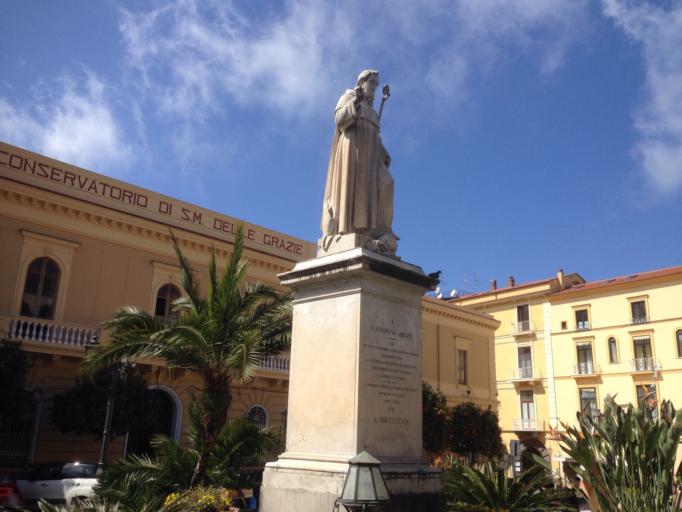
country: IT
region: Campania
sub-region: Provincia di Napoli
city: Sorrento
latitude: 40.6271
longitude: 14.3747
